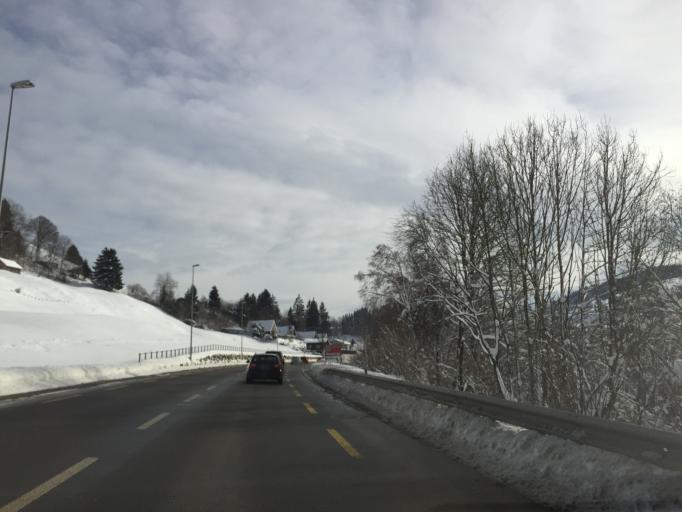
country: CH
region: Schwyz
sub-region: Bezirk Hoefe
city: Schindellegi
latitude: 47.1537
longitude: 8.7278
